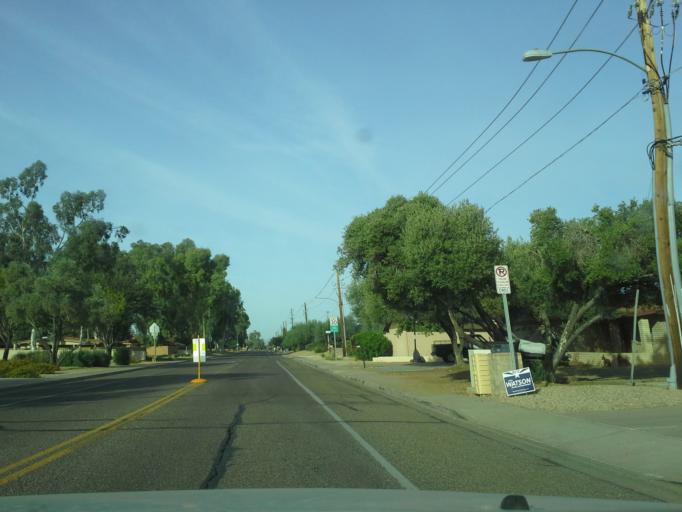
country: US
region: Arizona
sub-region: Maricopa County
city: Glendale
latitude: 33.6257
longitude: -112.0774
